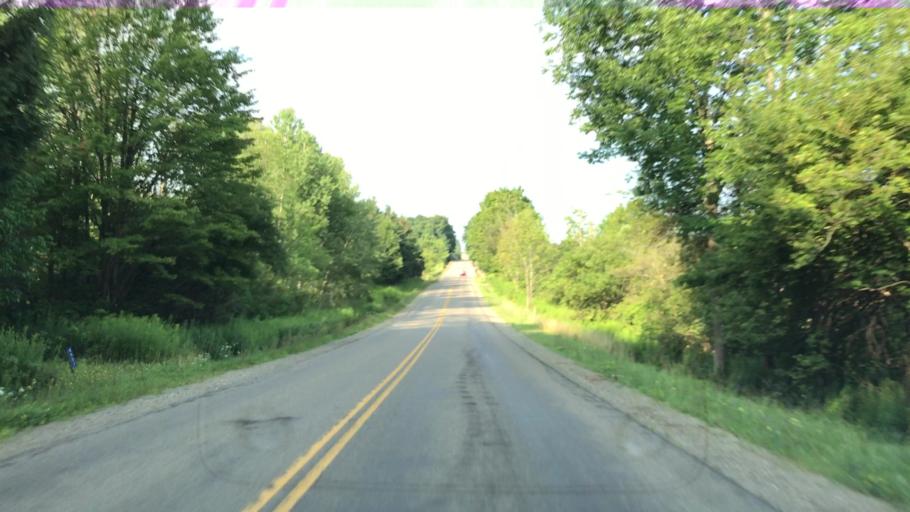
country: US
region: New York
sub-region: Chautauqua County
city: Brocton
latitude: 42.3081
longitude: -79.3795
